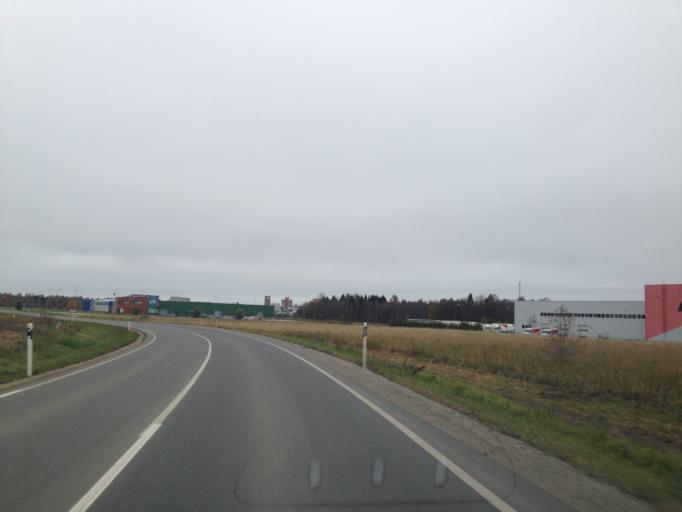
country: EE
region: Harju
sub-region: Harku vald
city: Tabasalu
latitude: 59.4168
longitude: 24.5434
